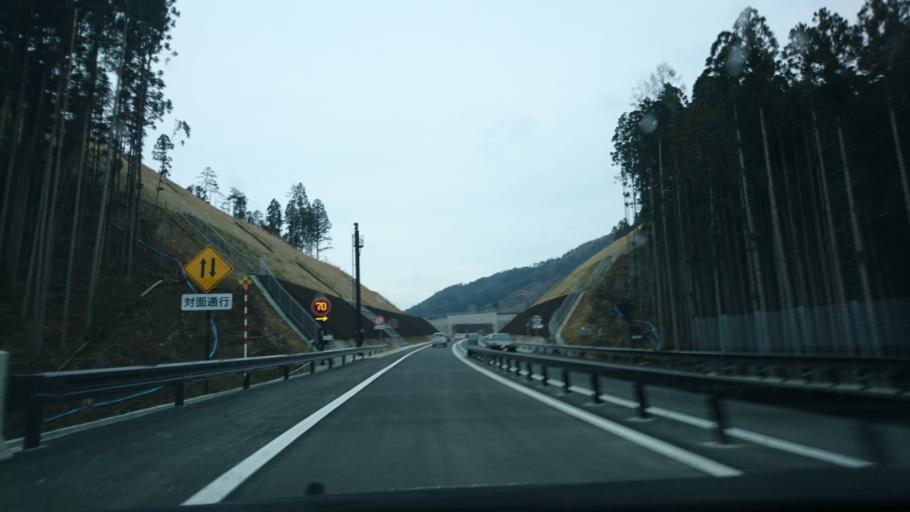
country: JP
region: Iwate
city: Ofunato
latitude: 38.9549
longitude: 141.6275
